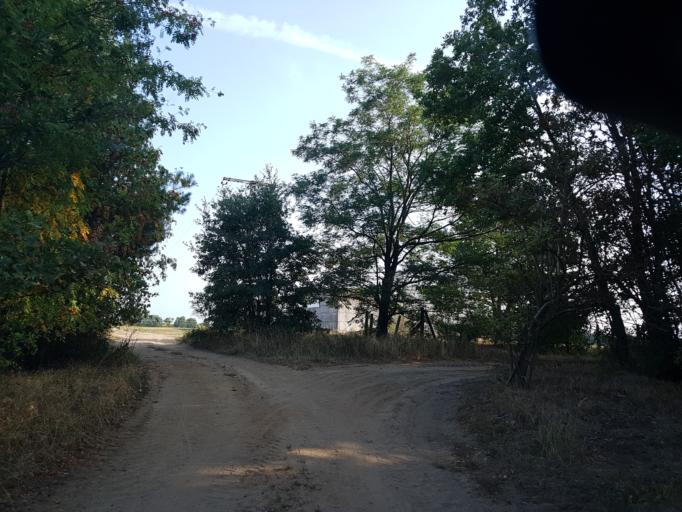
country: DE
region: Saxony-Anhalt
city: Klieken
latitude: 51.9727
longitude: 12.3434
